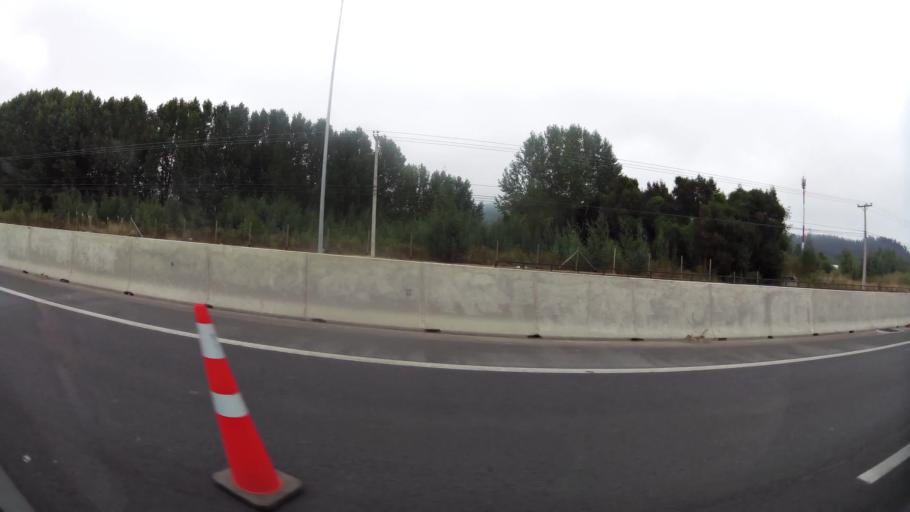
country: CL
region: Biobio
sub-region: Provincia de Concepcion
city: Concepcion
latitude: -36.8186
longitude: -73.0093
